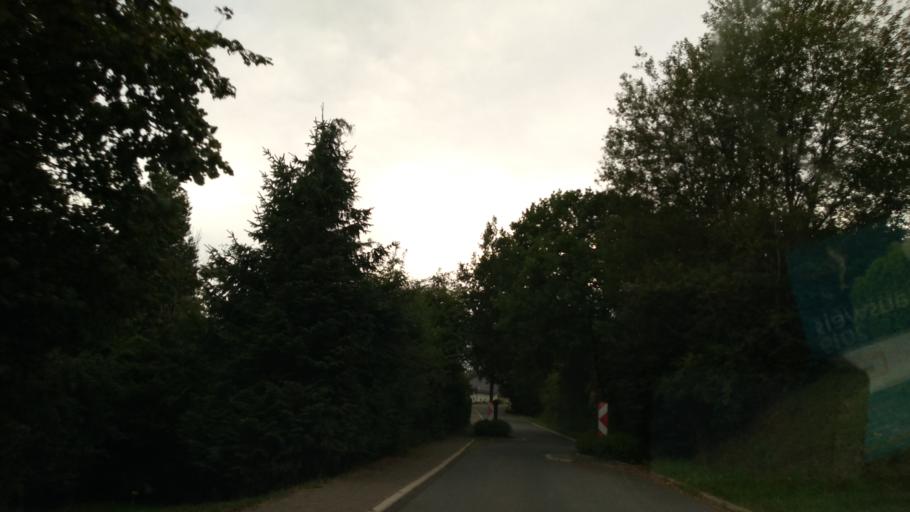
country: DE
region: North Rhine-Westphalia
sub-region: Regierungsbezirk Arnsberg
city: Herscheid
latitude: 51.1826
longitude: 7.7522
